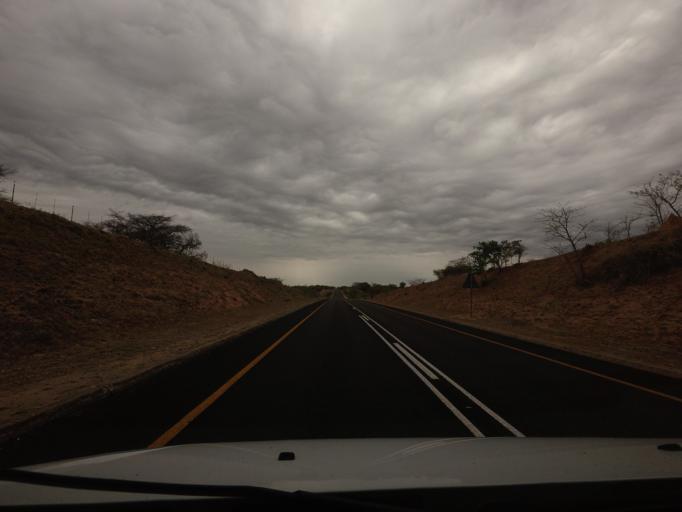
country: ZA
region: Limpopo
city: Thulamahashi
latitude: -24.5678
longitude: 31.0848
